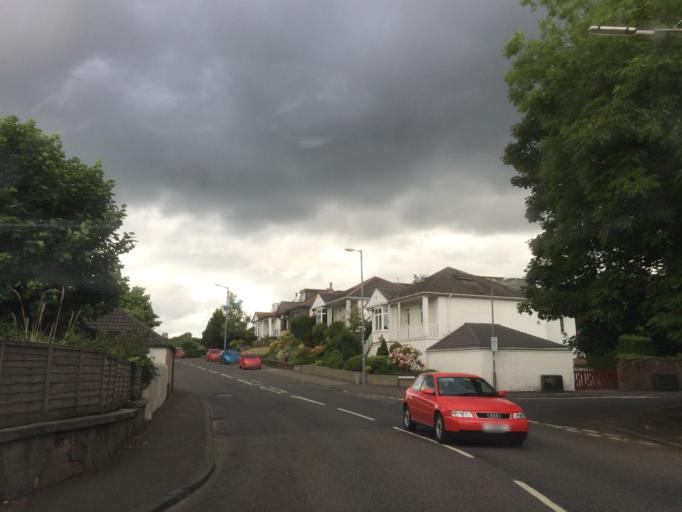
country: GB
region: Scotland
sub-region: East Renfrewshire
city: Giffnock
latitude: 55.8110
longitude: -4.2807
